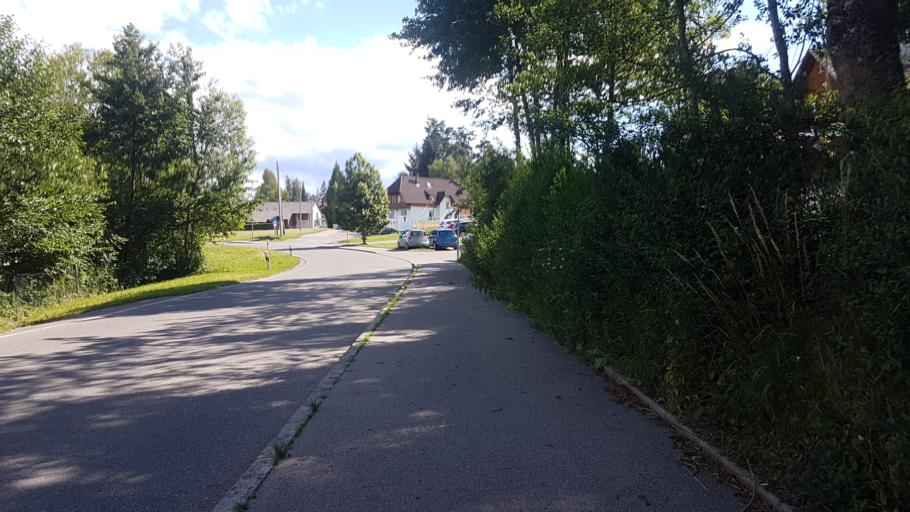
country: DE
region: Baden-Wuerttemberg
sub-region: Freiburg Region
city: Konigsfeld im Schwarzwald
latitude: 48.1420
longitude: 8.4027
